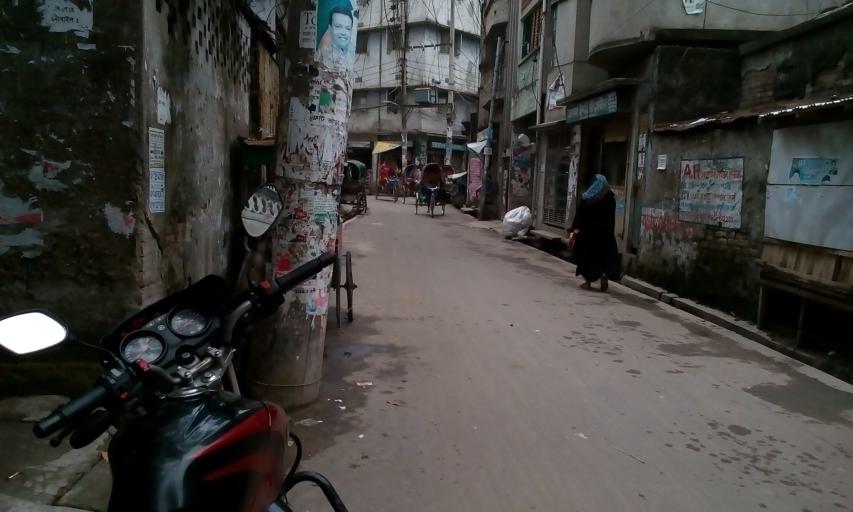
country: BD
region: Dhaka
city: Azimpur
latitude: 23.7214
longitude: 90.3834
